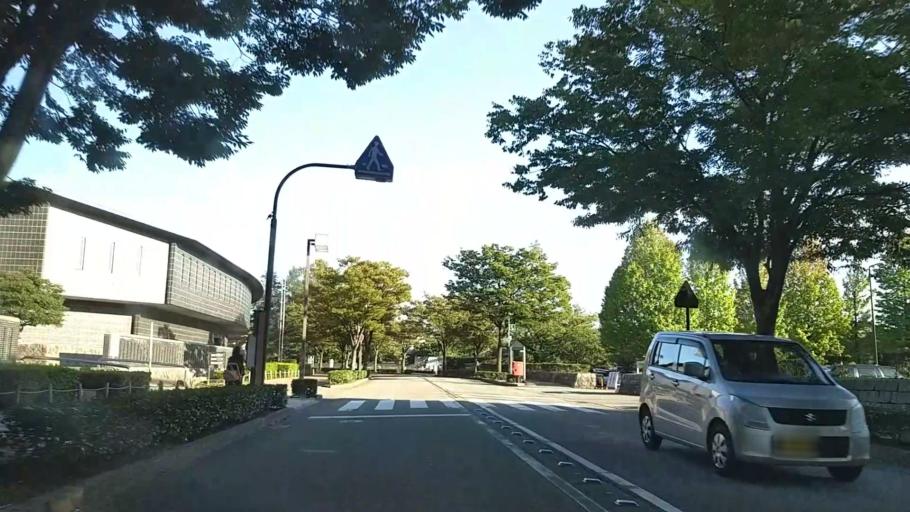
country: JP
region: Ishikawa
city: Kanazawa-shi
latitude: 36.5588
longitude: 136.6637
